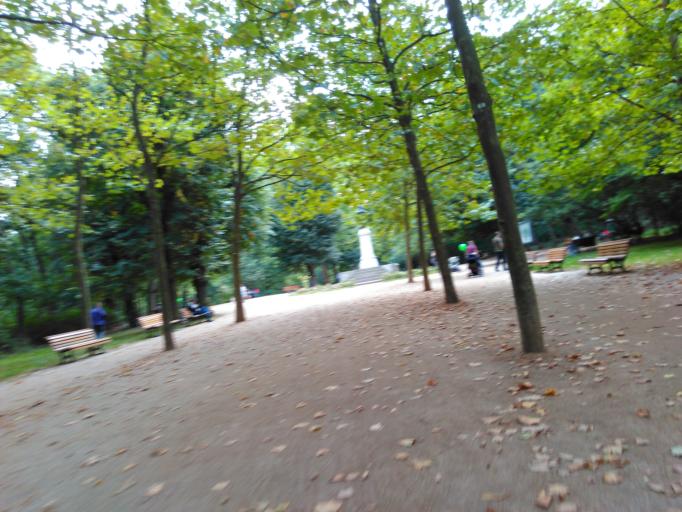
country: DE
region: Berlin
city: Prenzlauer Berg Bezirk
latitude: 52.5261
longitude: 13.4350
